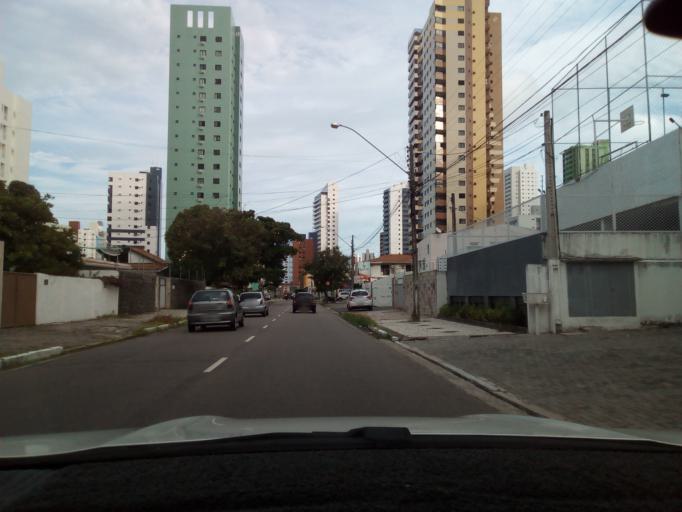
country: BR
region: Paraiba
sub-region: Joao Pessoa
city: Joao Pessoa
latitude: -7.1049
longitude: -34.8344
